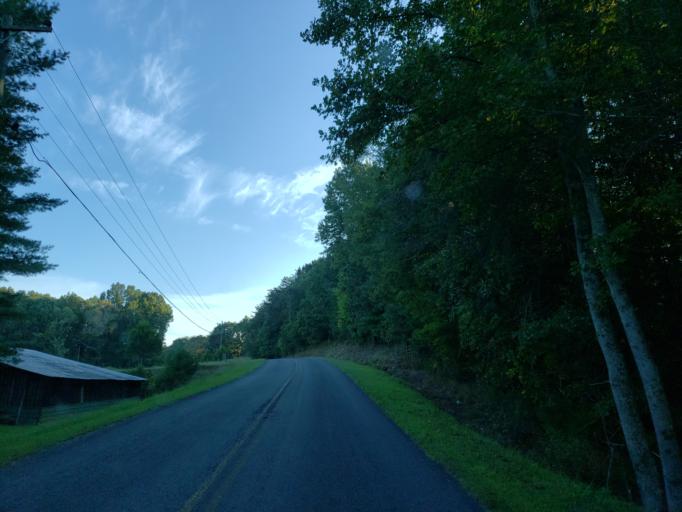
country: US
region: Georgia
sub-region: Gilmer County
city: Ellijay
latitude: 34.6632
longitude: -84.3364
